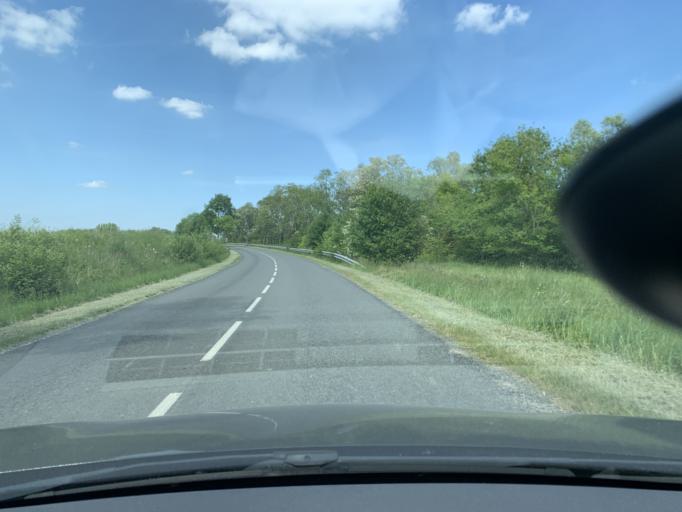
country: FR
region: Nord-Pas-de-Calais
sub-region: Departement du Pas-de-Calais
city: Marquion
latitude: 50.2321
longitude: 3.0896
